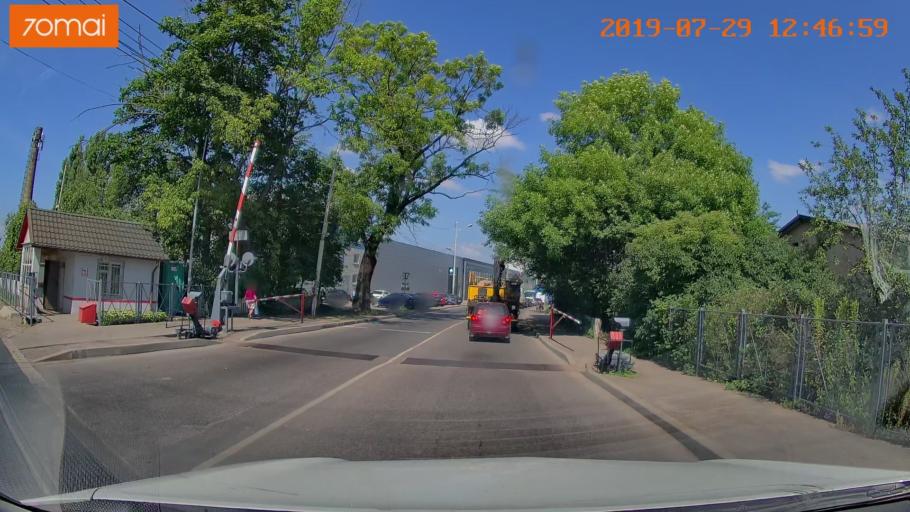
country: RU
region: Kaliningrad
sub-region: Gorod Kaliningrad
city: Kaliningrad
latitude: 54.6821
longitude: 20.5348
